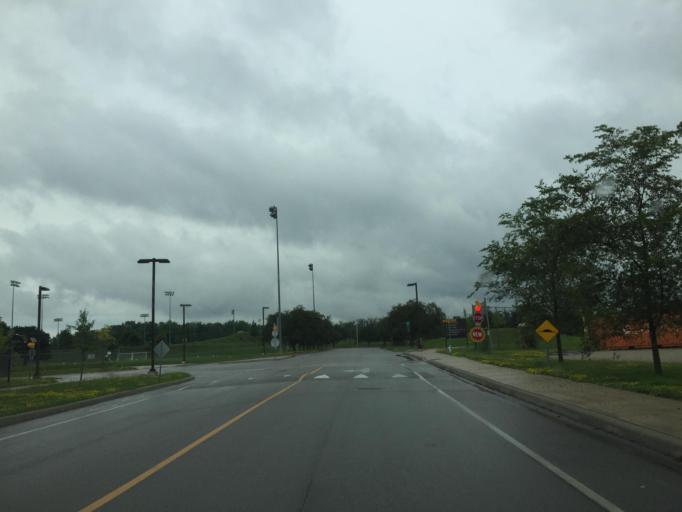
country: CA
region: Ontario
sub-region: Wellington County
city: Guelph
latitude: 43.5342
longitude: -80.2175
